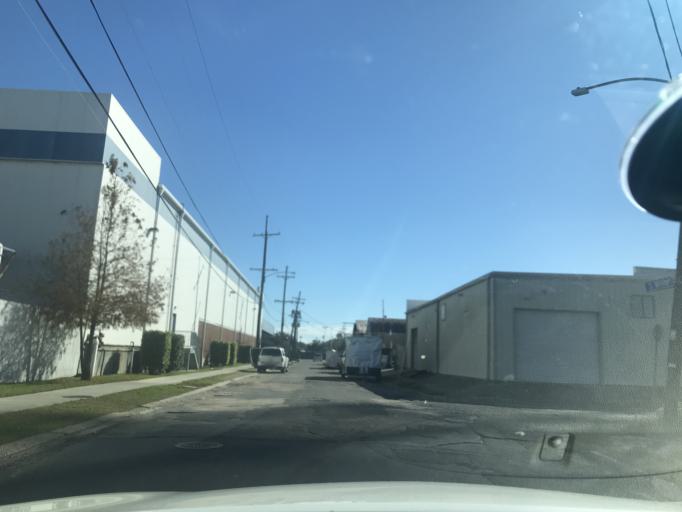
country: US
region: Louisiana
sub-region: Orleans Parish
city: New Orleans
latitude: 29.9552
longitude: -90.0986
